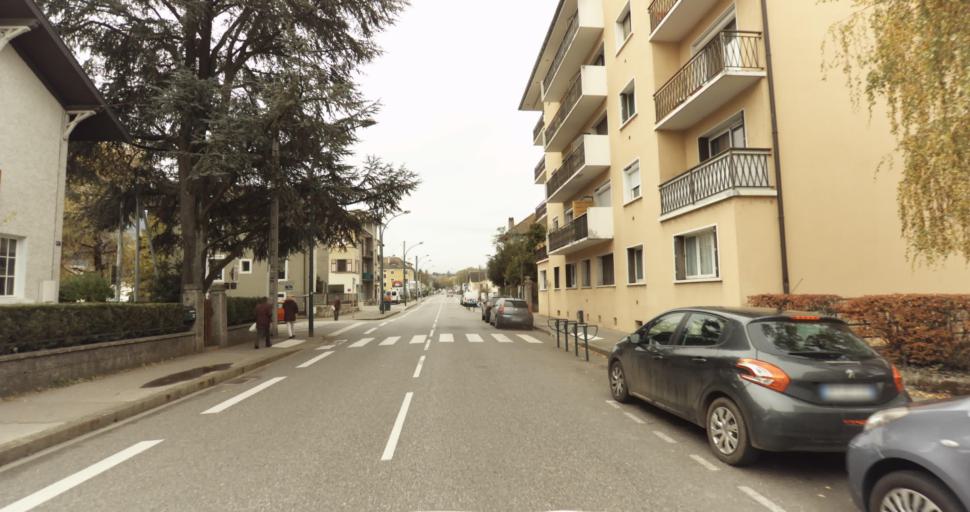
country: FR
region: Rhone-Alpes
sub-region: Departement de la Haute-Savoie
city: Annecy
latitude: 45.8940
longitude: 6.1183
